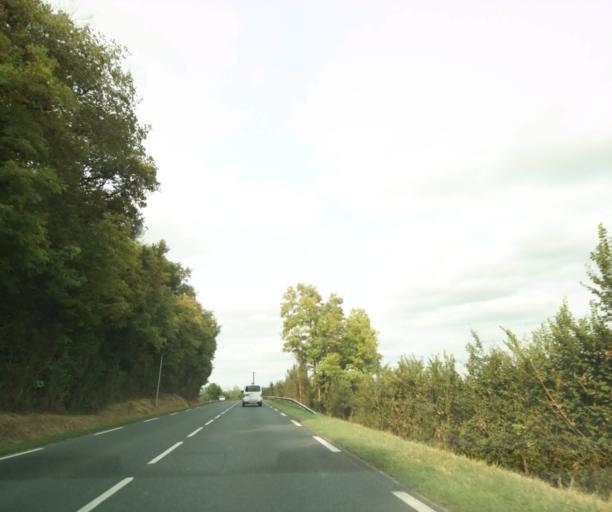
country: FR
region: Centre
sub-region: Departement de l'Indre
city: Clion
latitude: 46.9525
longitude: 1.2154
